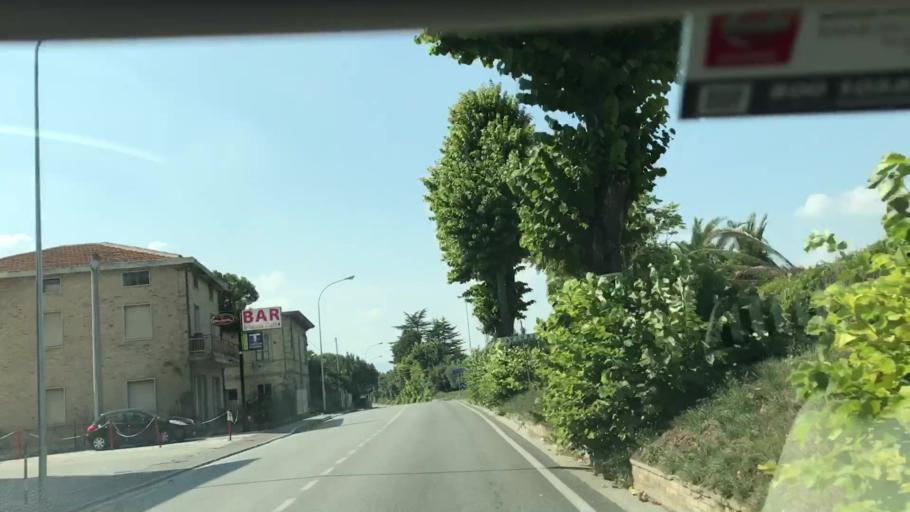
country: IT
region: The Marches
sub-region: Provincia di Ascoli Piceno
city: Stella
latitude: 42.8848
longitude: 13.8029
